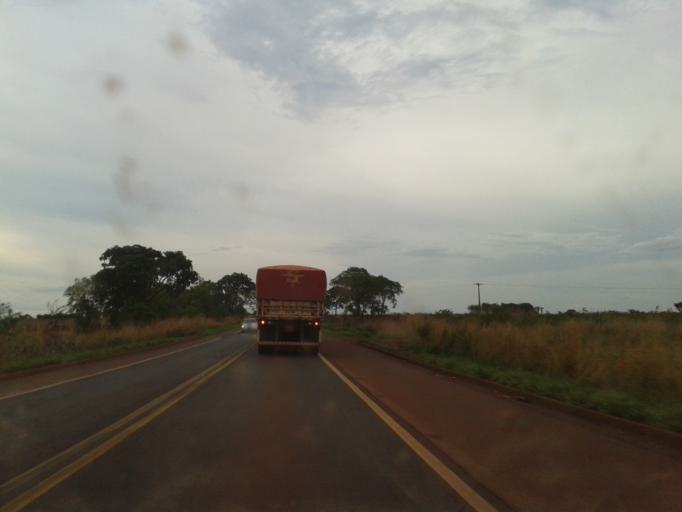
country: BR
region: Goias
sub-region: Santa Helena De Goias
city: Santa Helena de Goias
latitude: -17.9506
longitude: -50.5110
